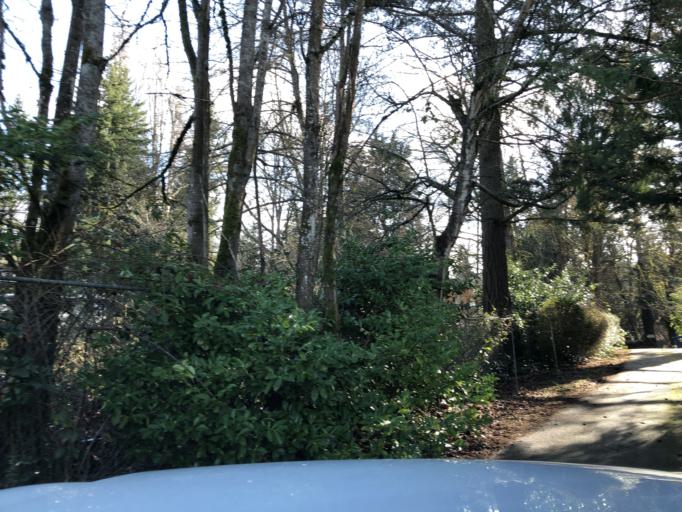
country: US
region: Washington
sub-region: King County
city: Lake Forest Park
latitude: 47.7225
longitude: -122.3060
